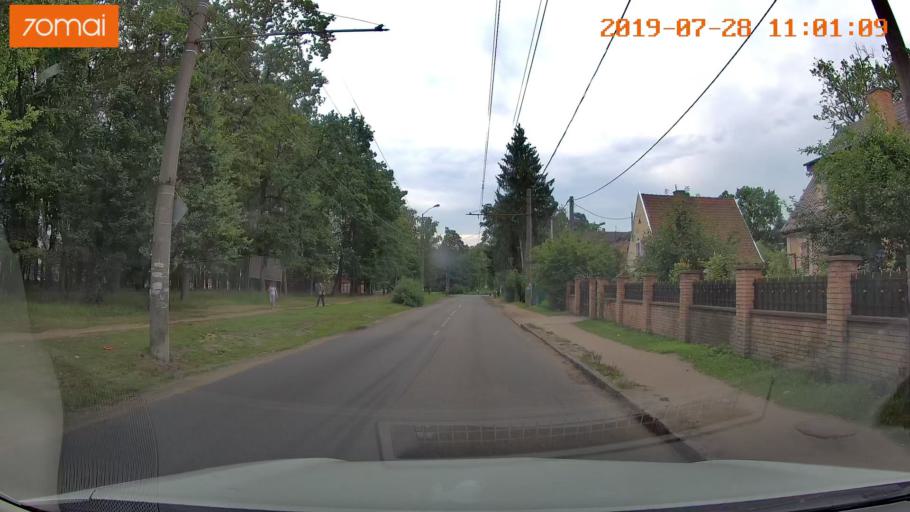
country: RU
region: Kaliningrad
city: Vzmorye
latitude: 54.7232
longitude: 20.3667
